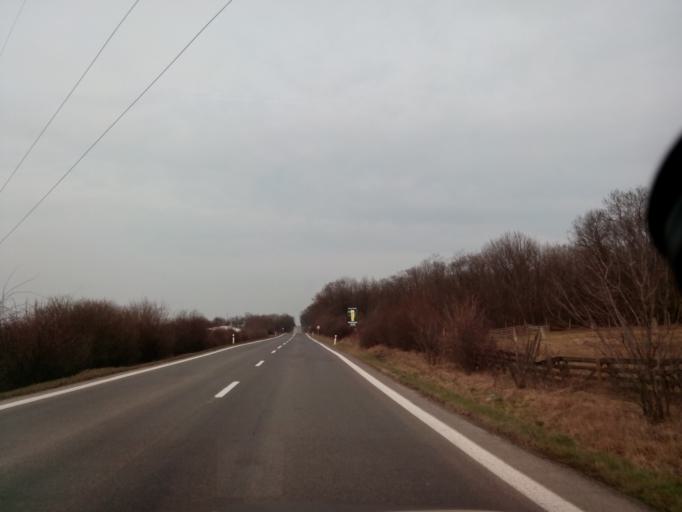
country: HU
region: Borsod-Abauj-Zemplen
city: Satoraljaujhely
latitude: 48.5001
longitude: 21.6522
